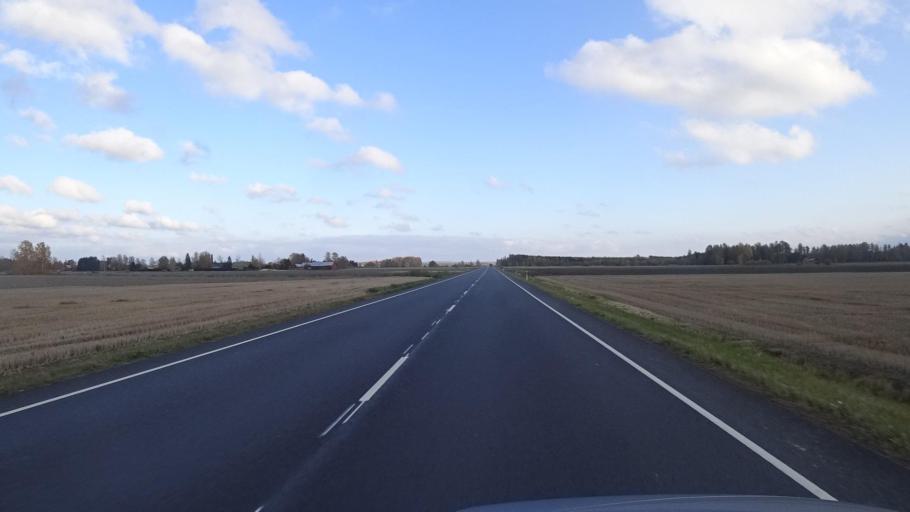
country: FI
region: Satakunta
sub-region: Rauma
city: Koeylioe
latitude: 61.0769
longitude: 22.2870
